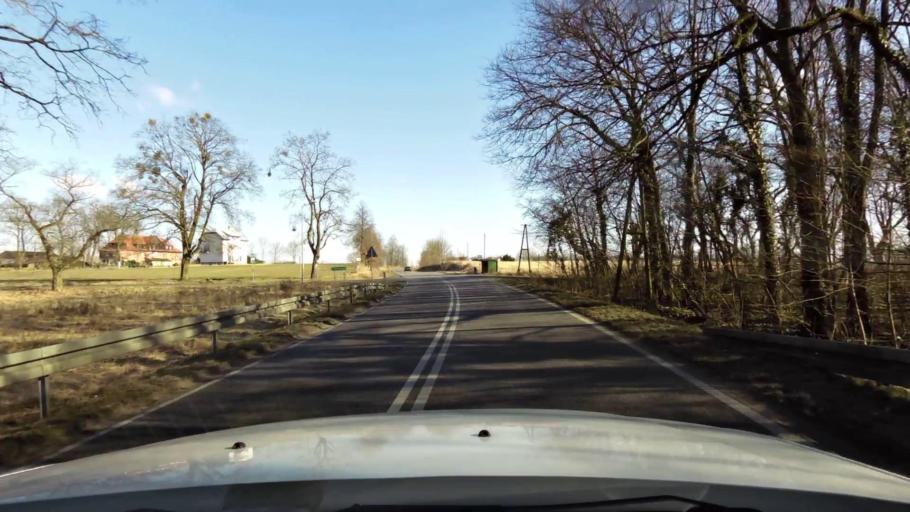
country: PL
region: West Pomeranian Voivodeship
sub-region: Powiat mysliborski
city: Barlinek
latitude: 52.9854
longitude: 15.1278
